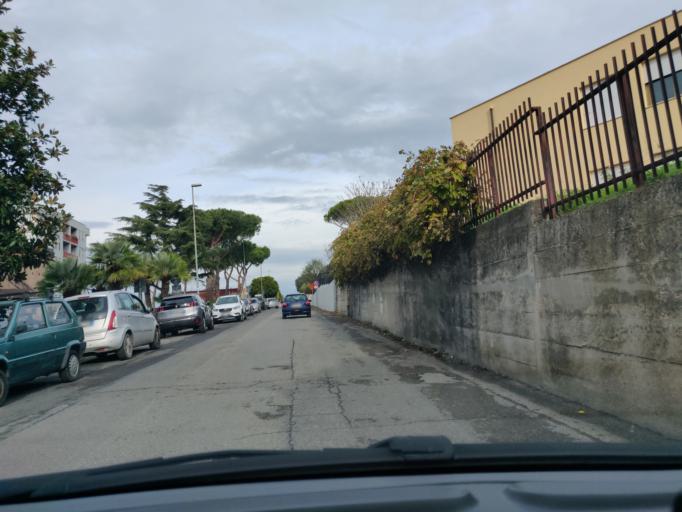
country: IT
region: Latium
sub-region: Citta metropolitana di Roma Capitale
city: Civitavecchia
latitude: 42.0970
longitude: 11.8146
